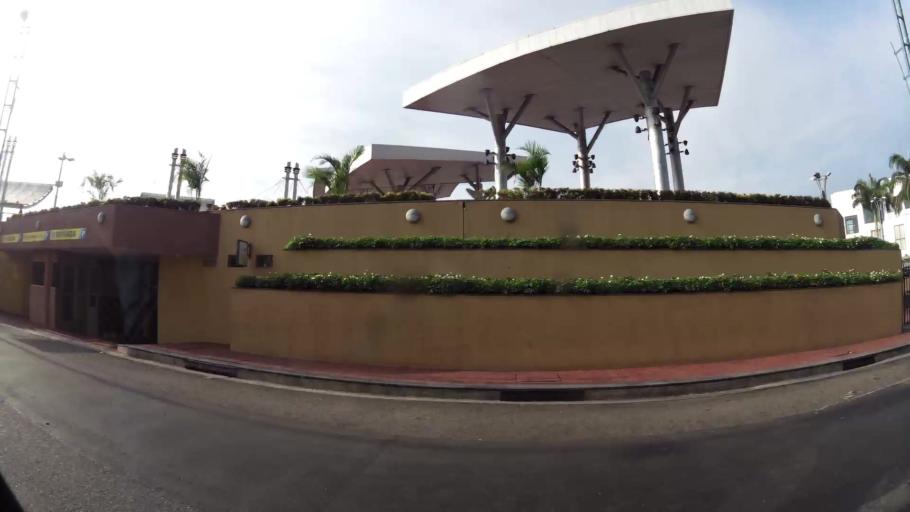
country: EC
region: Guayas
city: Guayaquil
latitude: -2.2006
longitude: -79.8820
